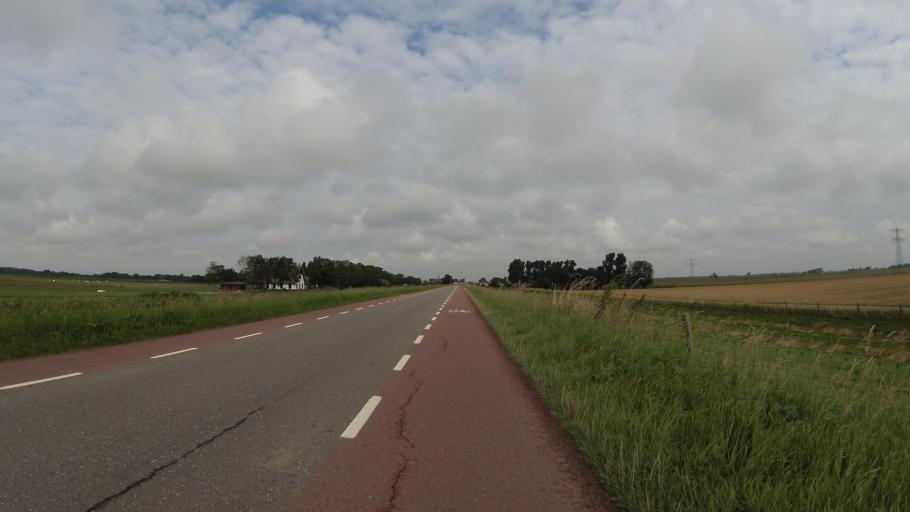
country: NL
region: North Holland
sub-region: Gemeente Schagen
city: Schagen
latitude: 52.8289
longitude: 4.8156
